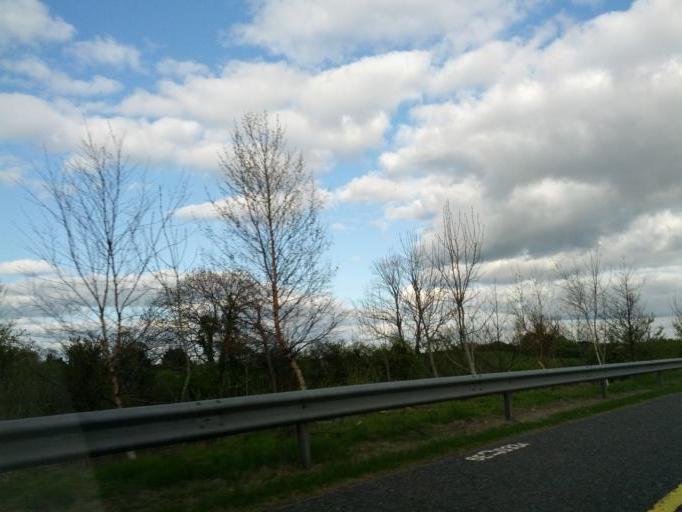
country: IE
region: Leinster
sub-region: An Iarmhi
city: Kilbeggan
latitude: 53.3722
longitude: -7.5416
